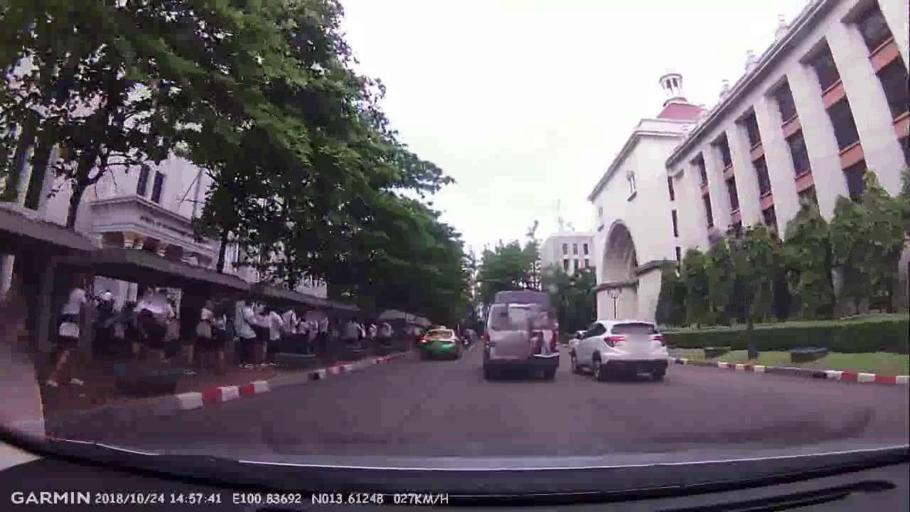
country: TH
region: Samut Prakan
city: Bang Sao Thong
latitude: 13.6126
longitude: 100.8369
